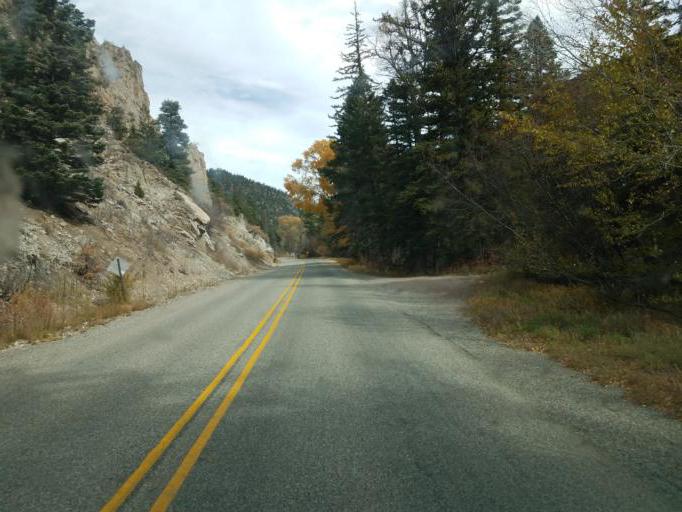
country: US
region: New Mexico
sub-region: Taos County
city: Arroyo Seco
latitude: 36.5516
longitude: -105.5410
